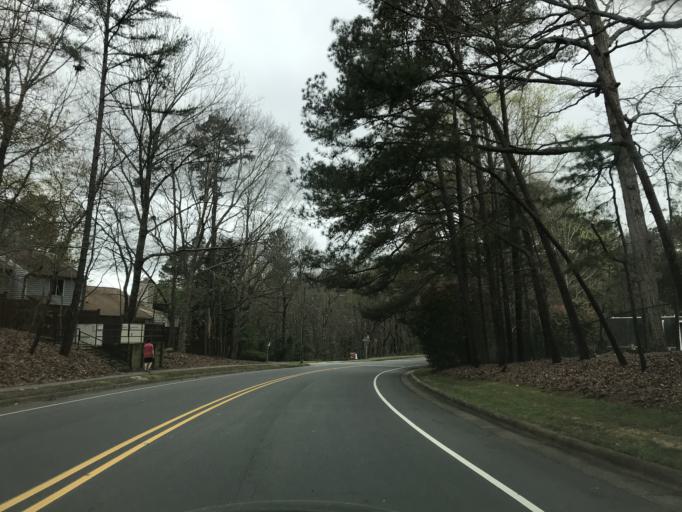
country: US
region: North Carolina
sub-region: Wake County
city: West Raleigh
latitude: 35.8744
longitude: -78.6466
